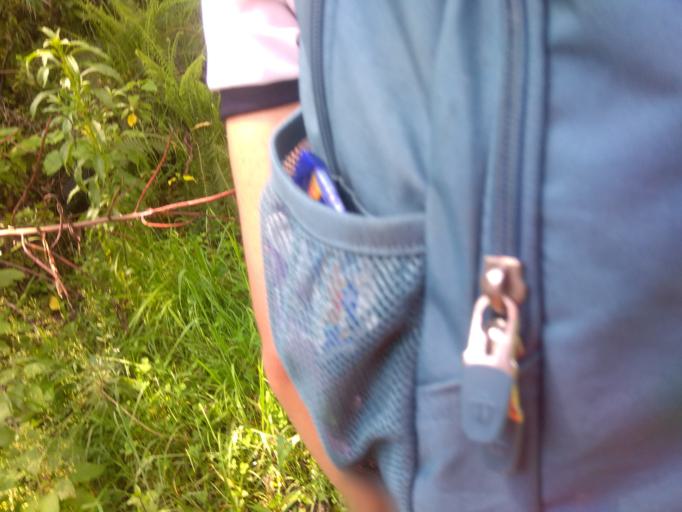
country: CO
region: Boyaca
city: Socha Viejo
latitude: 5.9793
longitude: -72.7235
